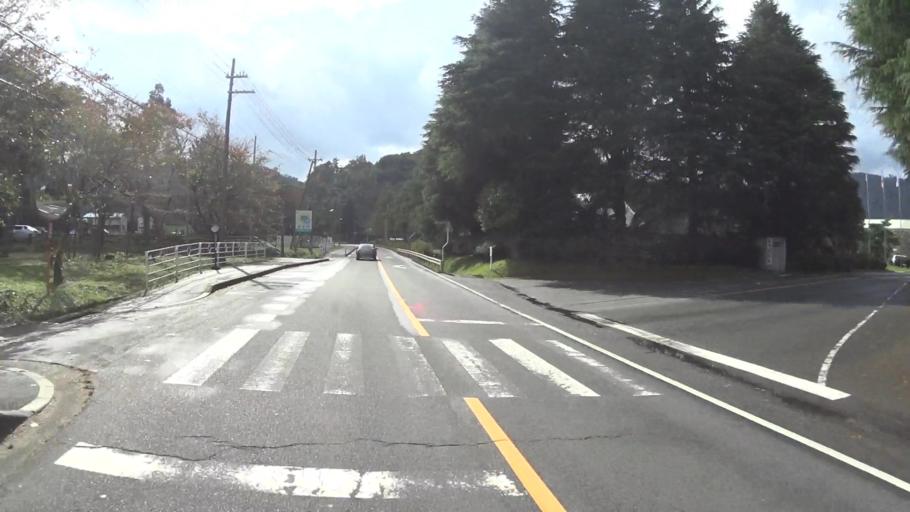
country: JP
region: Kyoto
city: Miyazu
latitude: 35.5576
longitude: 135.1533
